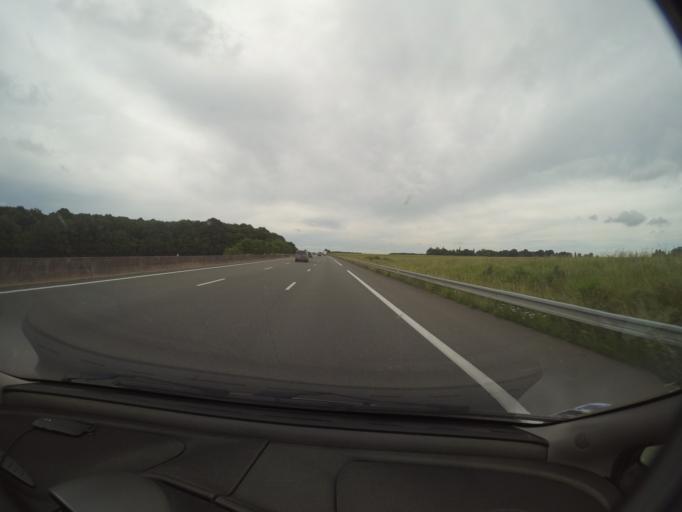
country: FR
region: Centre
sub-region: Departement d'Eure-et-Loir
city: Brou
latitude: 48.2587
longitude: 1.1345
